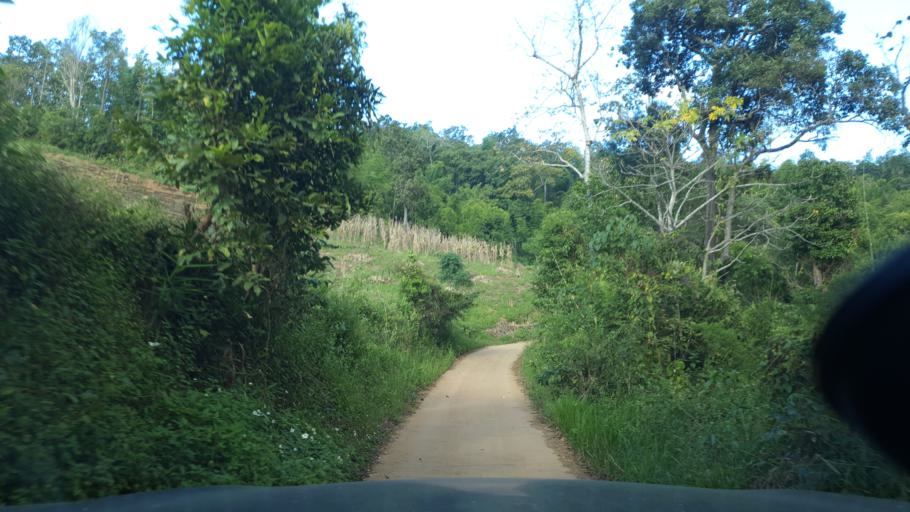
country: TH
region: Chiang Mai
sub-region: Amphoe Chiang Dao
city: Chiang Dao
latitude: 19.4069
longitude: 98.8328
